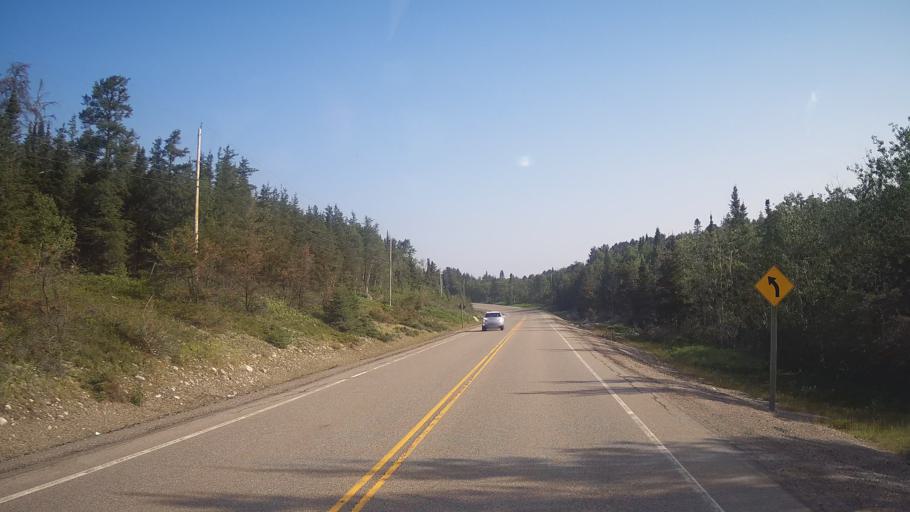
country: CA
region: Ontario
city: Rayside-Balfour
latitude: 46.7099
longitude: -81.5617
